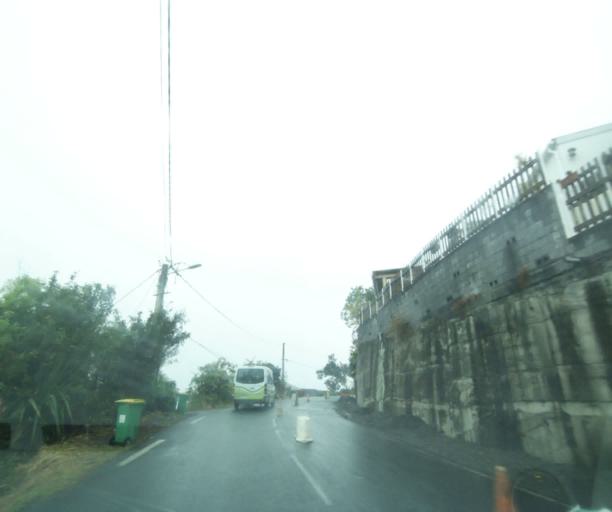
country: RE
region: Reunion
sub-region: Reunion
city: Saint-Paul
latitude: -21.0005
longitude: 55.3252
